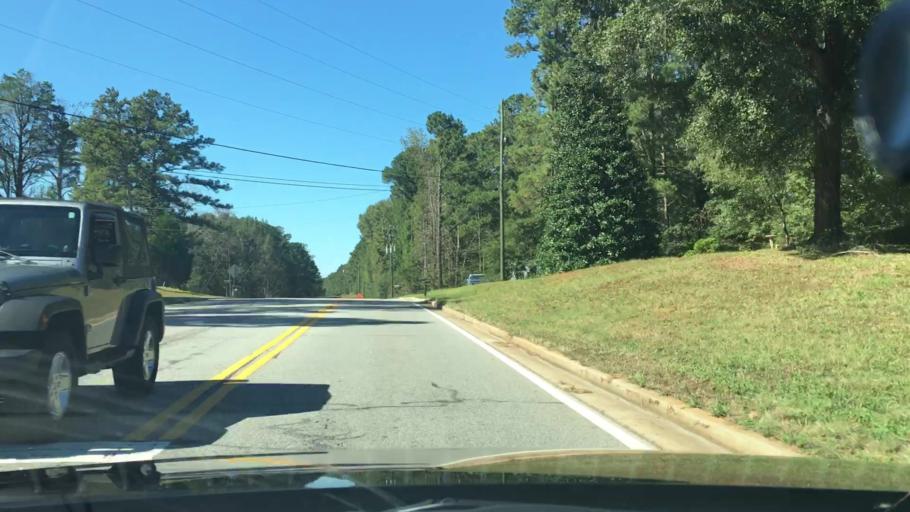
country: US
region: Georgia
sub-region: Fayette County
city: Tyrone
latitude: 33.4517
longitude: -84.6573
